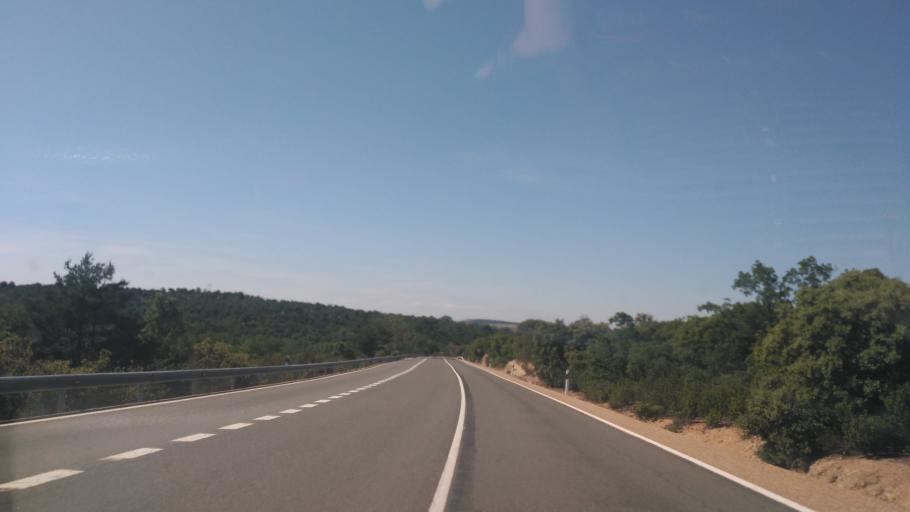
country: ES
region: Castille and Leon
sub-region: Provincia de Zamora
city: Corrales
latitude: 41.3008
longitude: -5.7255
